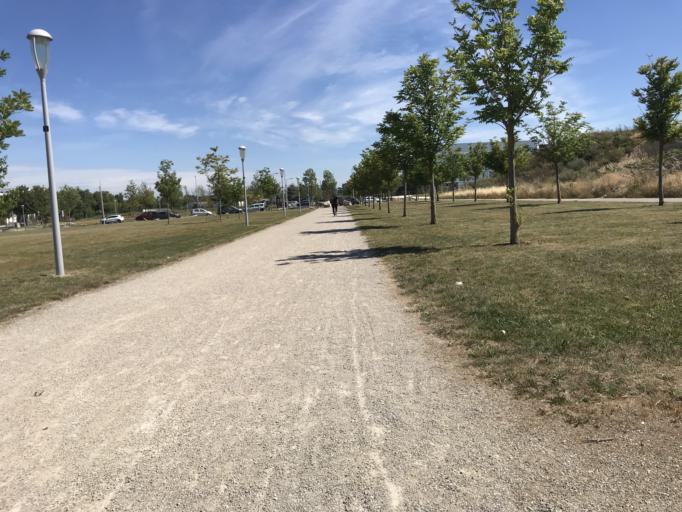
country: FR
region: Champagne-Ardenne
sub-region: Departement de la Marne
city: Bezannes
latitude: 49.2167
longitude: 3.9978
